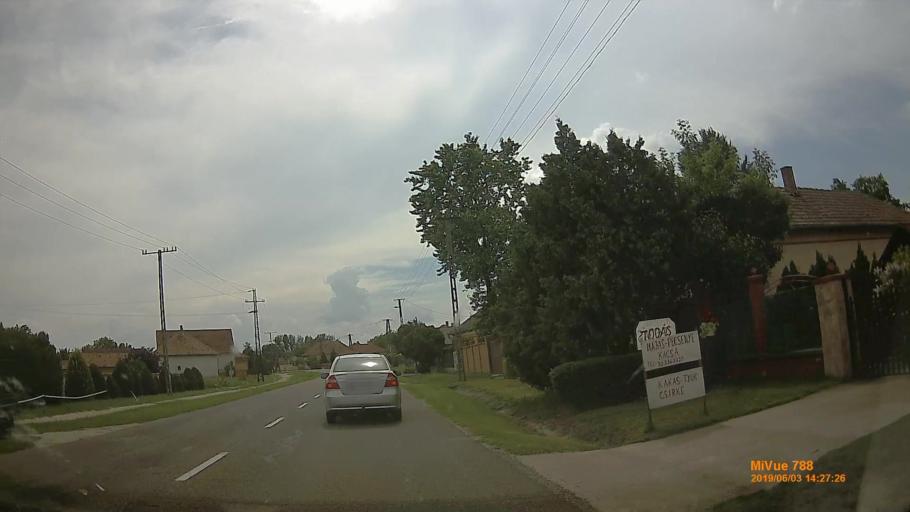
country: HU
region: Bacs-Kiskun
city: Tiszakecske
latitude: 46.9856
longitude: 20.1178
